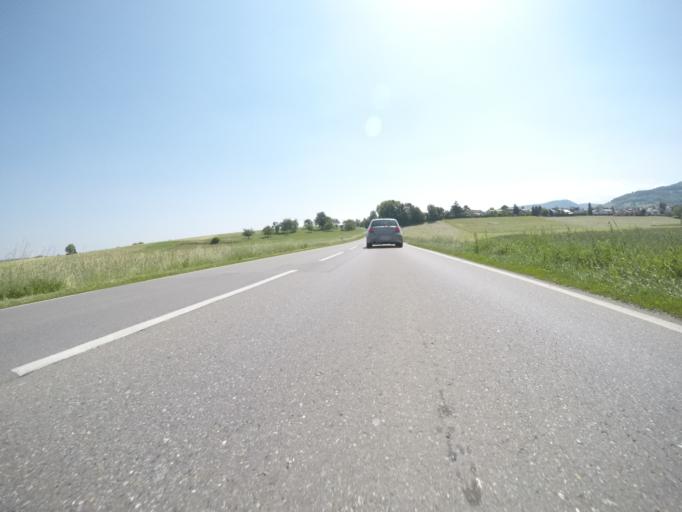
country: DE
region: Baden-Wuerttemberg
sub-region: Regierungsbezirk Stuttgart
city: Dettingen unter Teck
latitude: 48.6184
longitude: 9.4596
